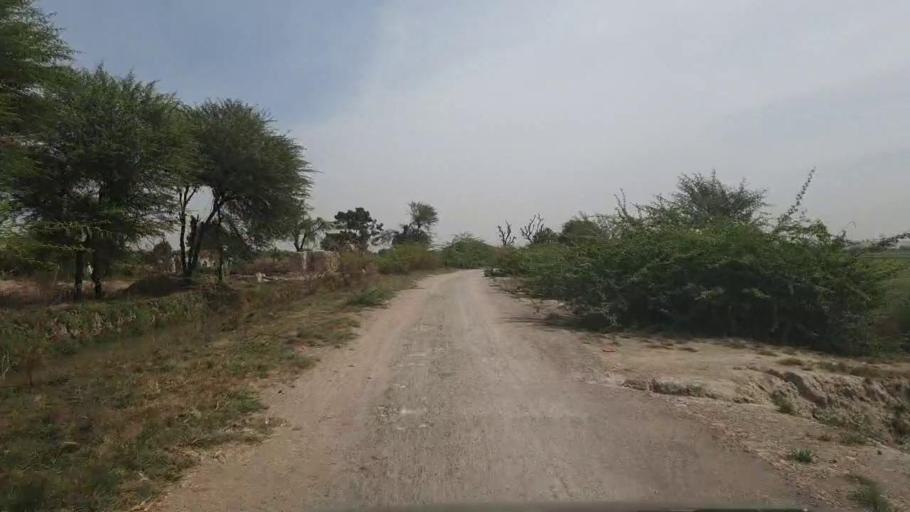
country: PK
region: Sindh
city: Umarkot
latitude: 25.2461
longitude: 69.7028
